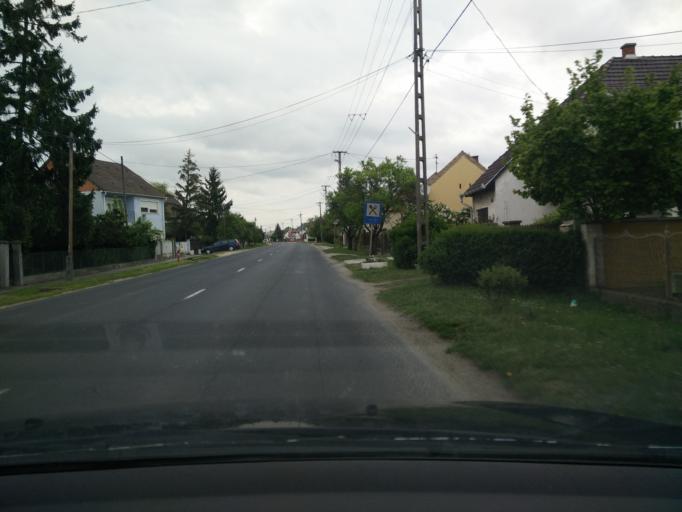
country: HU
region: Gyor-Moson-Sopron
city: Tet
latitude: 47.5181
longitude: 17.5175
